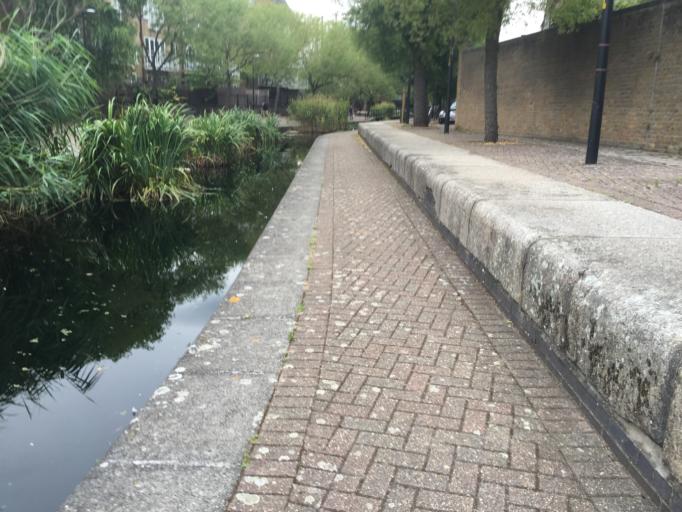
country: GB
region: England
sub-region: Greater London
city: Bethnal Green
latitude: 51.5012
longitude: -0.0452
